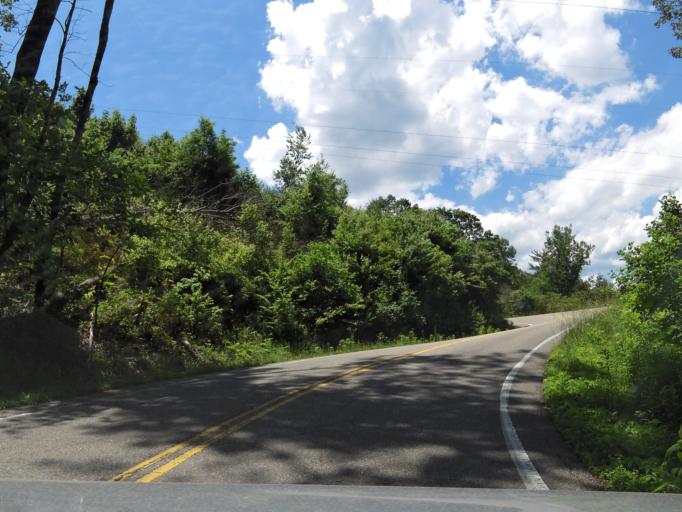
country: US
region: North Carolina
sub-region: Graham County
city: Robbinsville
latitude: 35.4896
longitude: -83.9305
